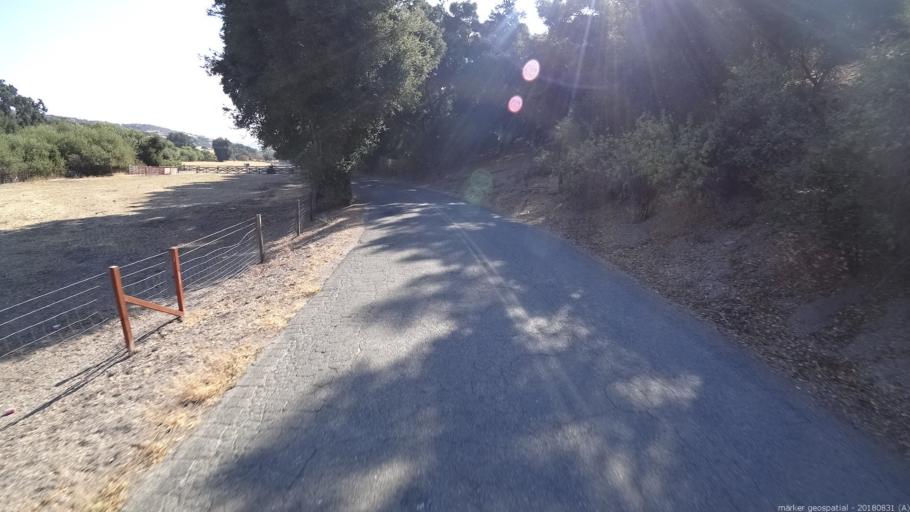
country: US
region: California
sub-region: Monterey County
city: King City
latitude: 36.1512
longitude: -121.1860
